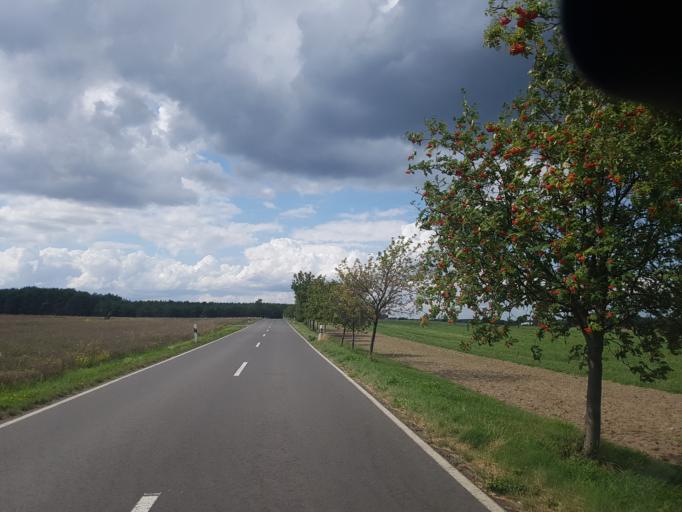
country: DE
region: Brandenburg
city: Schlieben
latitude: 51.6840
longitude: 13.3467
